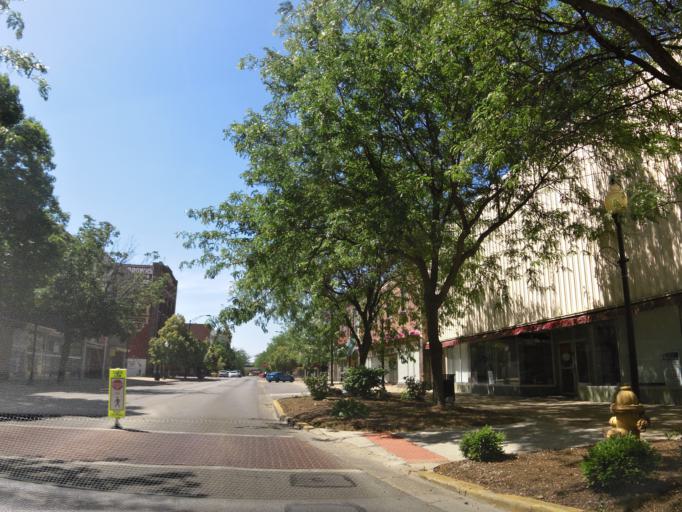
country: US
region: Illinois
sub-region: Vermilion County
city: Danville
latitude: 40.1272
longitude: -87.6301
